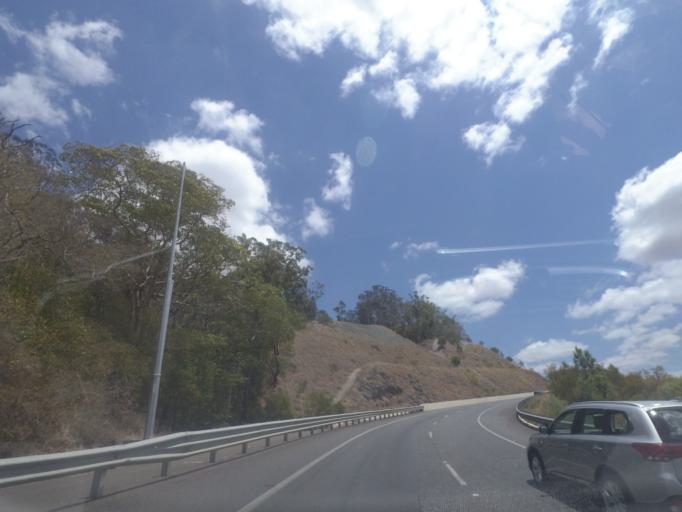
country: AU
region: Queensland
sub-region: Toowoomba
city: East Toowoomba
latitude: -27.5712
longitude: 151.9820
